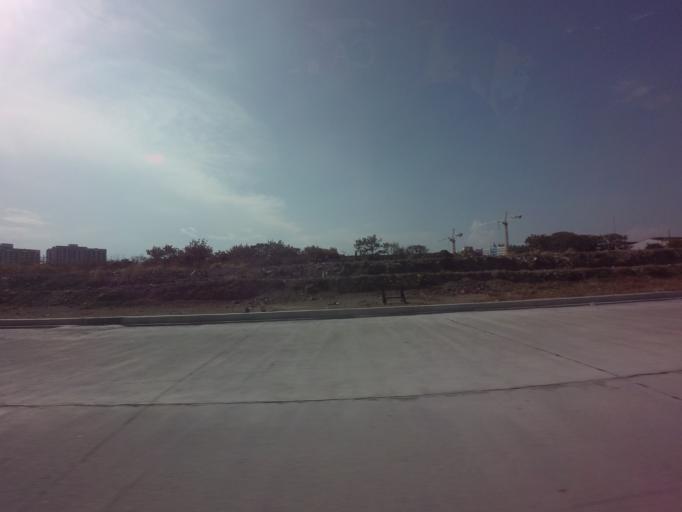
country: PH
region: Calabarzon
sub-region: Province of Rizal
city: Taguig
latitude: 14.5045
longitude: 121.0379
